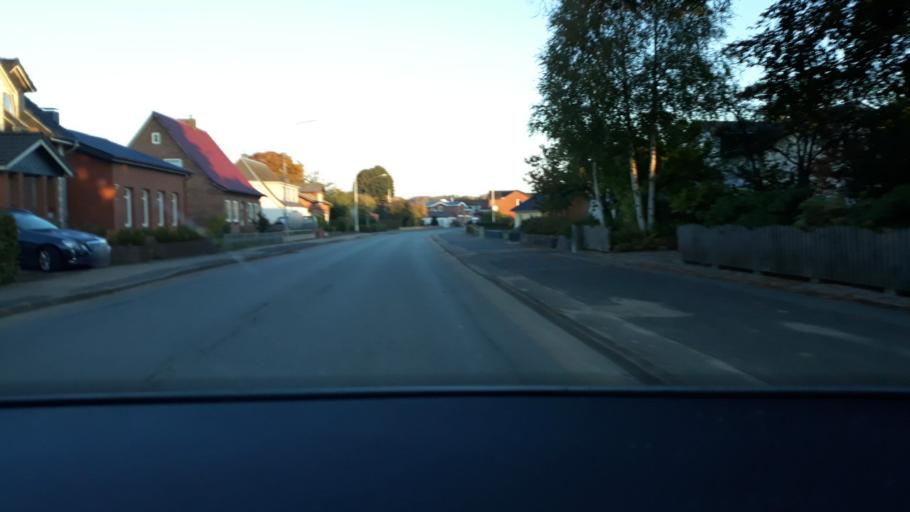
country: DE
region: Schleswig-Holstein
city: Satrup
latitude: 54.6859
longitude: 9.6033
